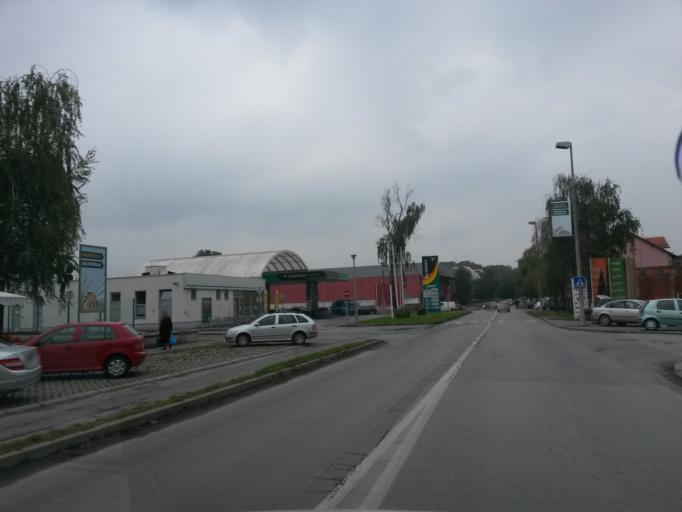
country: HR
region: Osjecko-Baranjska
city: Viskovci
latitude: 45.3188
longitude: 18.4159
